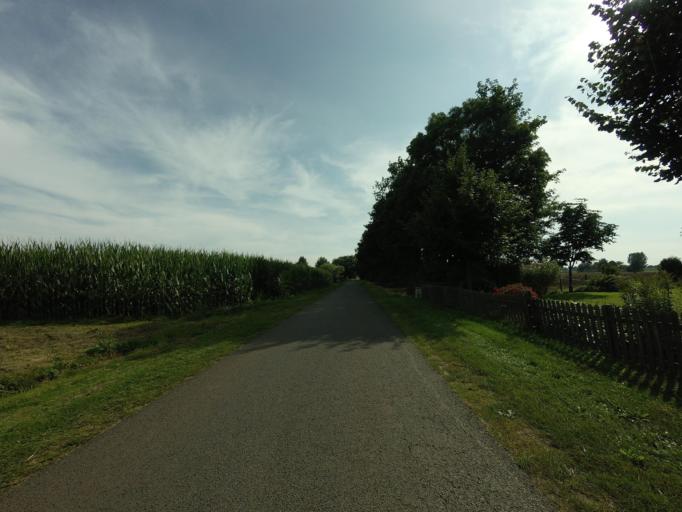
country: NL
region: Drenthe
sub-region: Gemeente Coevorden
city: Dalen
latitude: 52.7009
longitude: 6.7315
